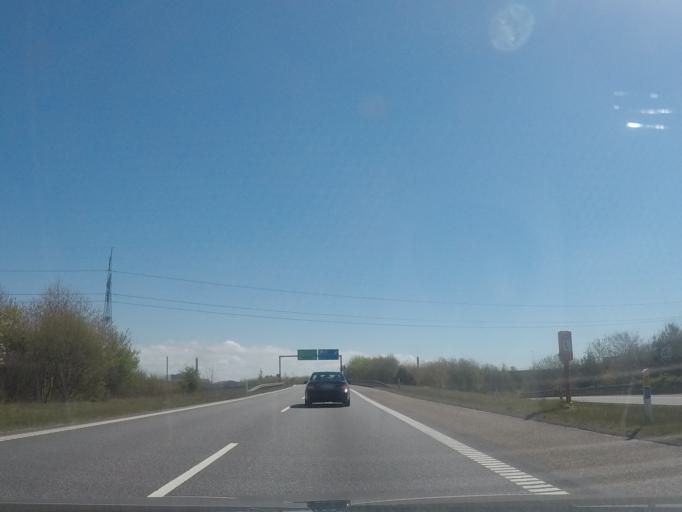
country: DK
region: South Denmark
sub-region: Assens Kommune
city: Vissenbjerg
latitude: 55.3988
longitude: 10.1534
